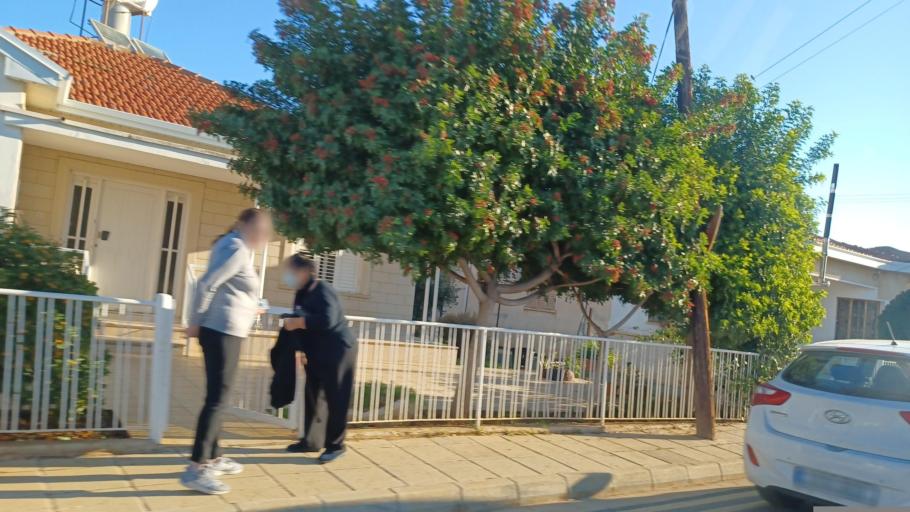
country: CY
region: Lefkosia
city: Astromeritis
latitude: 35.1421
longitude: 33.0394
